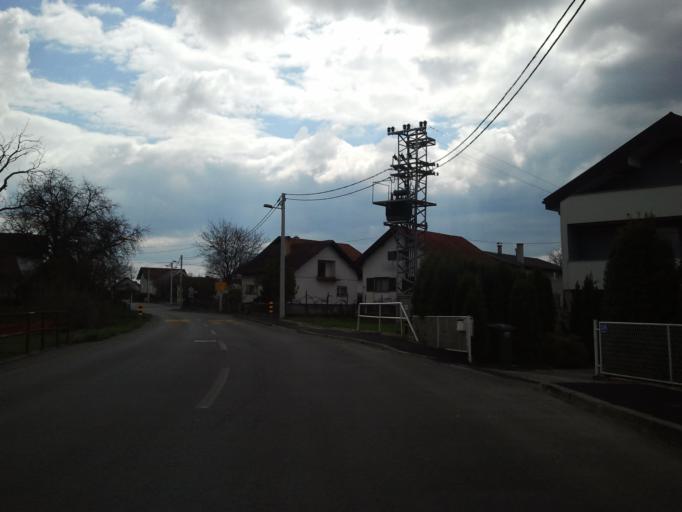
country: HR
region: Grad Zagreb
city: Zadvorsko
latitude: 45.7169
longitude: 15.9405
